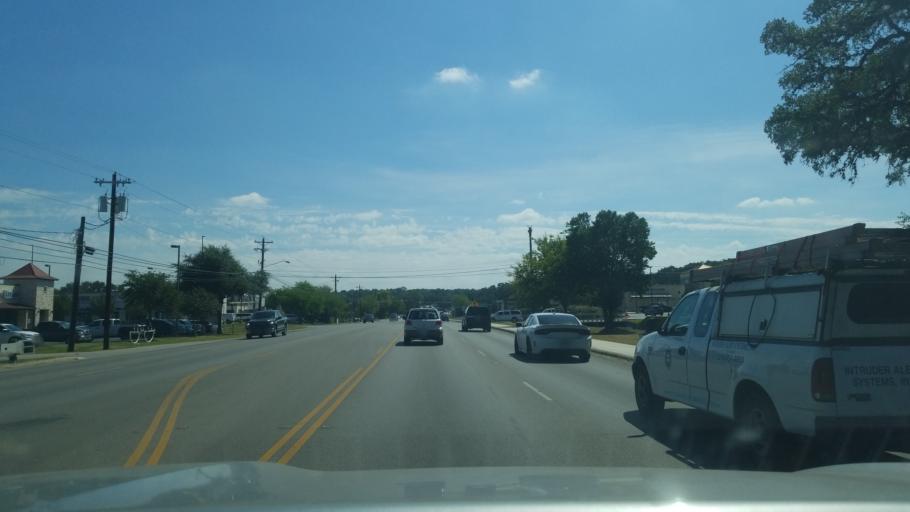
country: US
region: Texas
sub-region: Kendall County
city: Boerne
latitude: 29.7766
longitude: -98.7258
